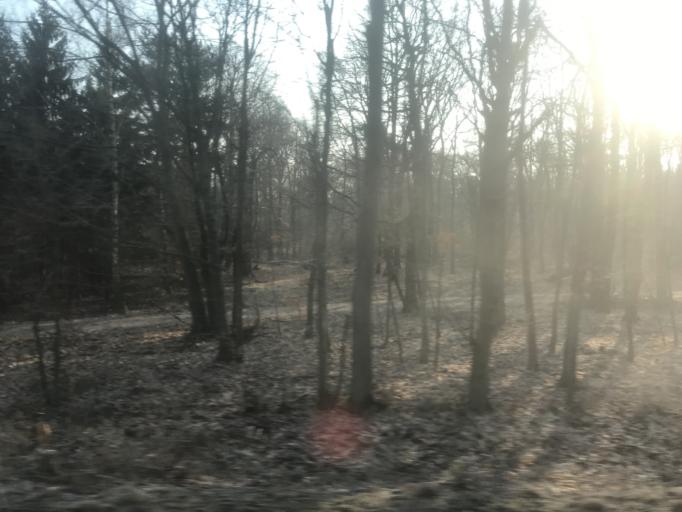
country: DE
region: Hesse
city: Kelsterbach
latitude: 50.0590
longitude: 8.5521
